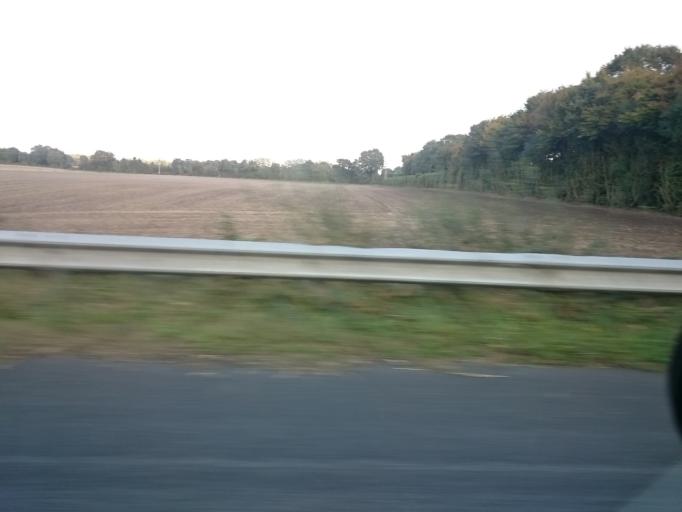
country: FR
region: Pays de la Loire
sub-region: Departement de la Loire-Atlantique
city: Jans
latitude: 47.6191
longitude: -1.6380
